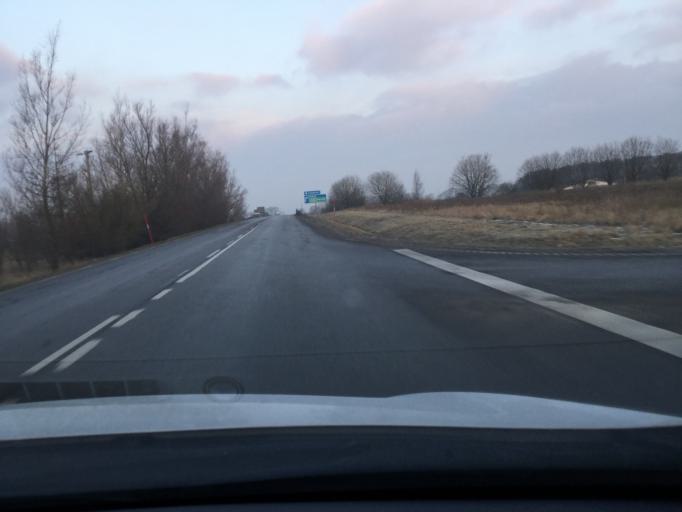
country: SE
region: Skane
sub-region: Hoors Kommun
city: Loberod
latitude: 55.7838
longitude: 13.4178
